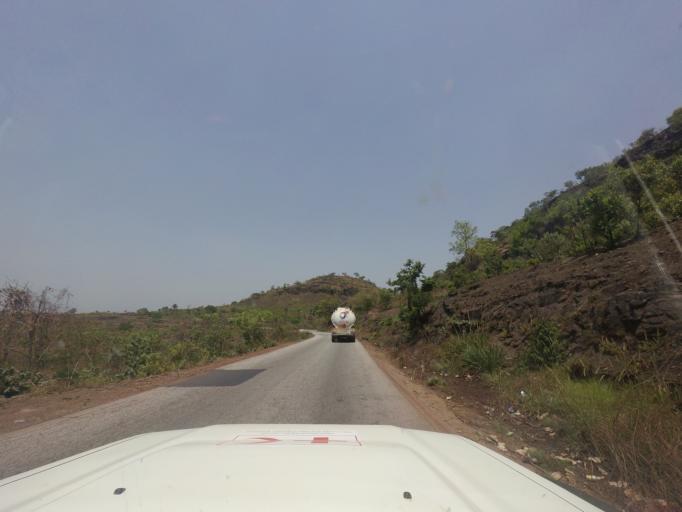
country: GN
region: Kindia
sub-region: Coyah
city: Coyah
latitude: 9.8355
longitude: -13.1329
